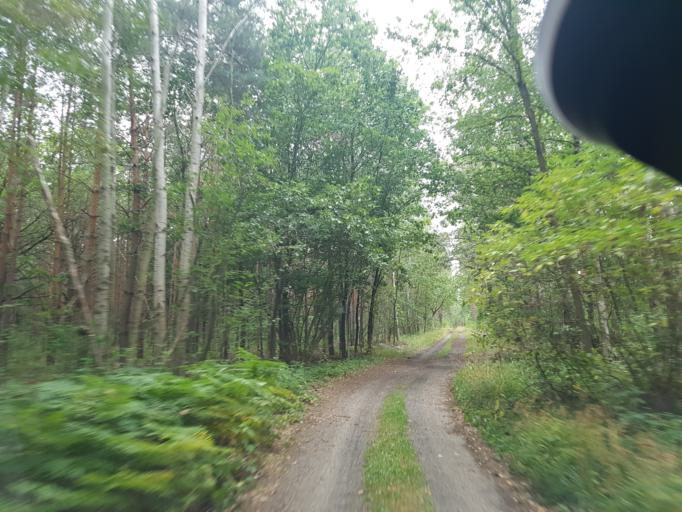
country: DE
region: Brandenburg
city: Ruckersdorf
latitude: 51.5986
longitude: 13.5709
